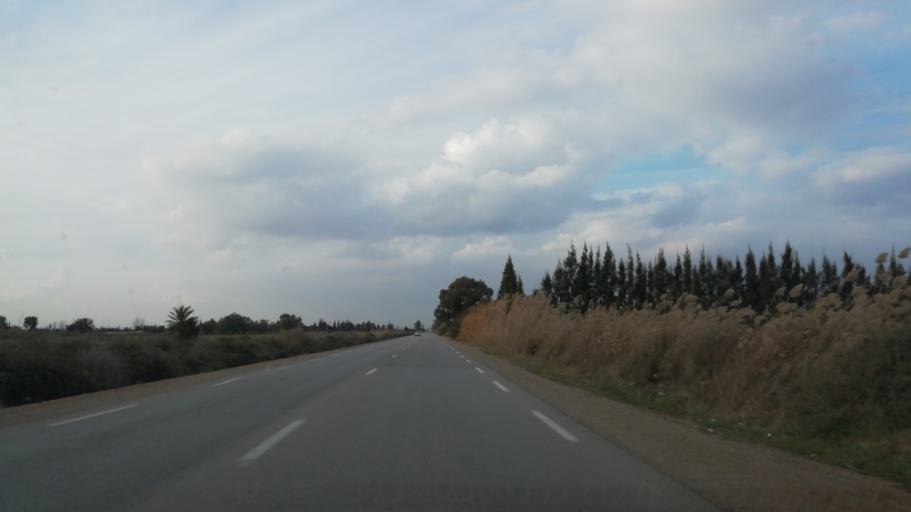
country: DZ
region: Mascara
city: Sig
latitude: 35.6740
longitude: -0.0053
